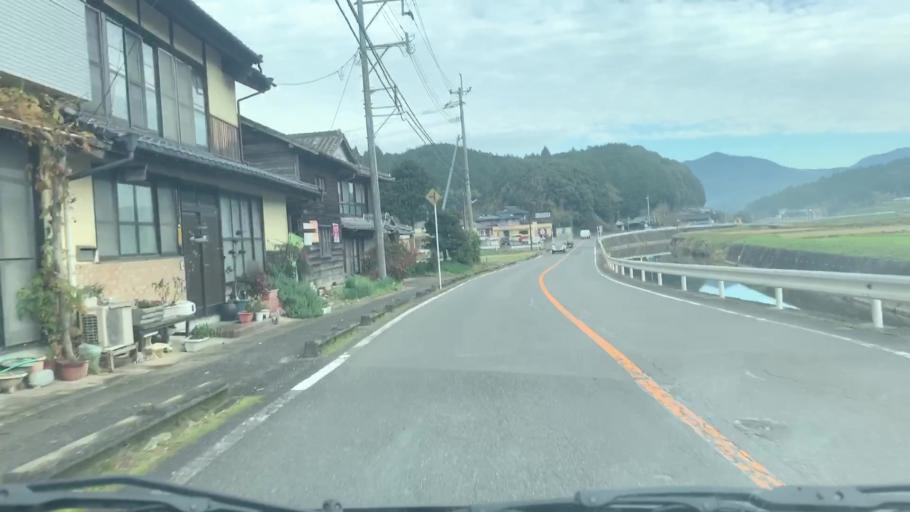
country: JP
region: Saga Prefecture
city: Takeocho-takeo
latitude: 33.2286
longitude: 129.9638
